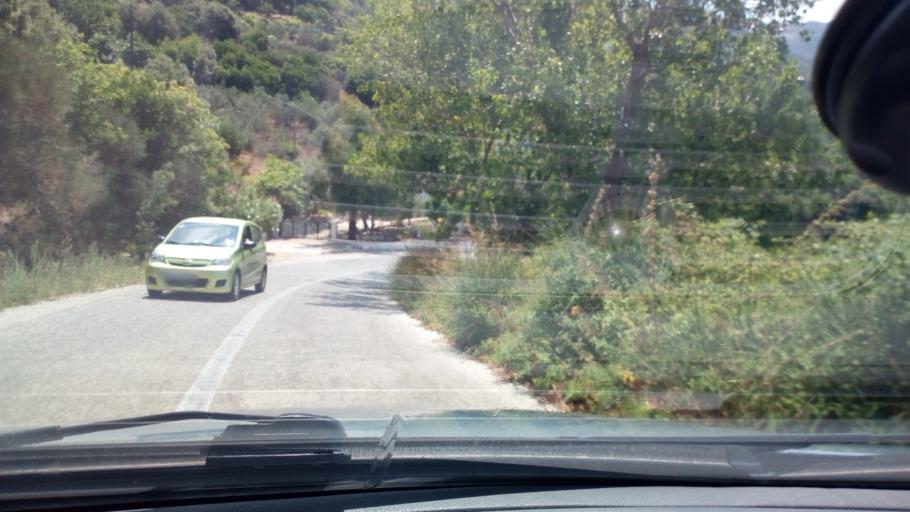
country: GR
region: North Aegean
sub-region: Nomos Samou
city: Agios Kirykos
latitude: 37.6428
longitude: 26.2601
